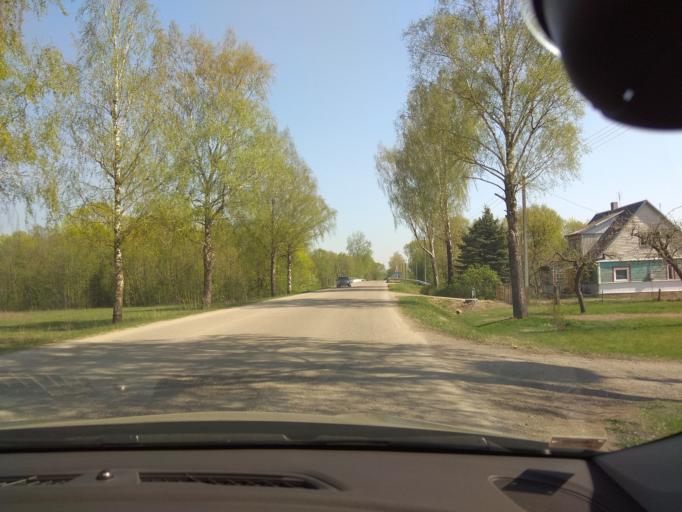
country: LT
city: Linkuva
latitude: 56.0258
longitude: 23.9601
